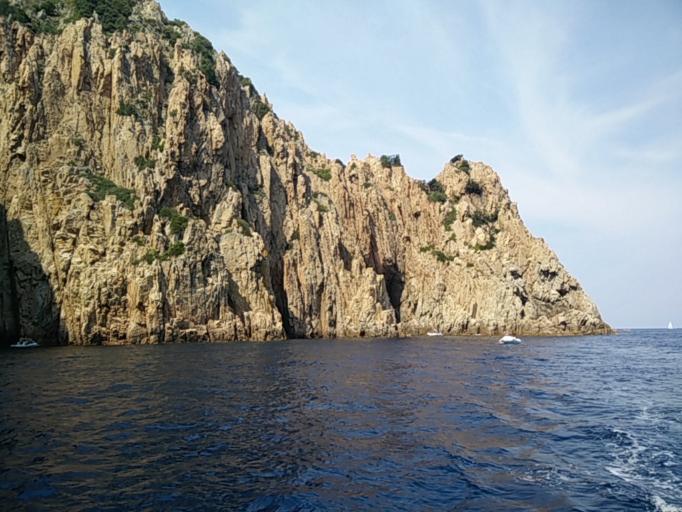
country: FR
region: Corsica
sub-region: Departement de la Corse-du-Sud
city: Cargese
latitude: 42.2394
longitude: 8.5516
